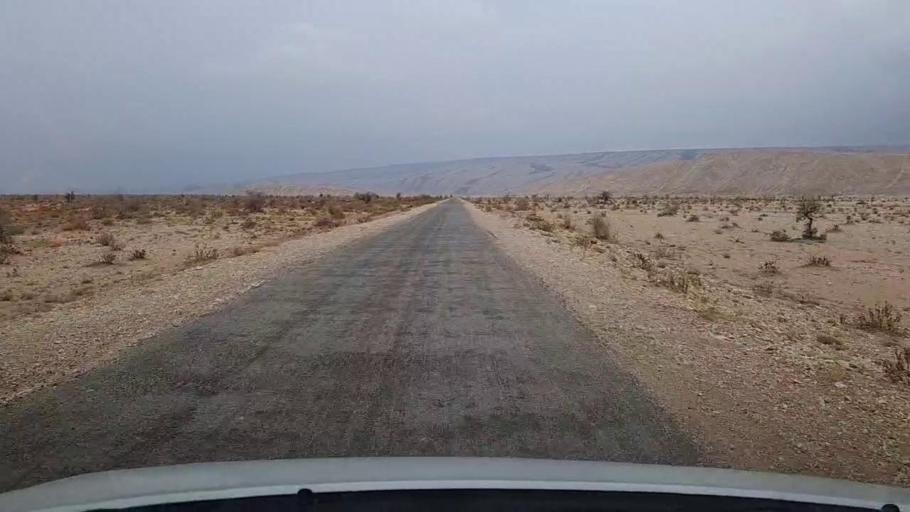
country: PK
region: Sindh
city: Sehwan
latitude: 26.2506
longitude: 67.7186
